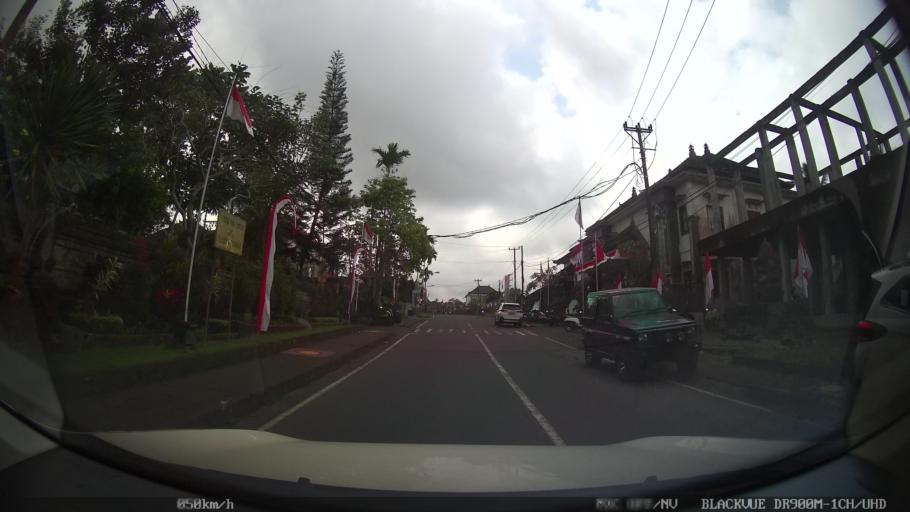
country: ID
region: Bali
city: Petang
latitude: -8.4021
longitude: 115.2185
